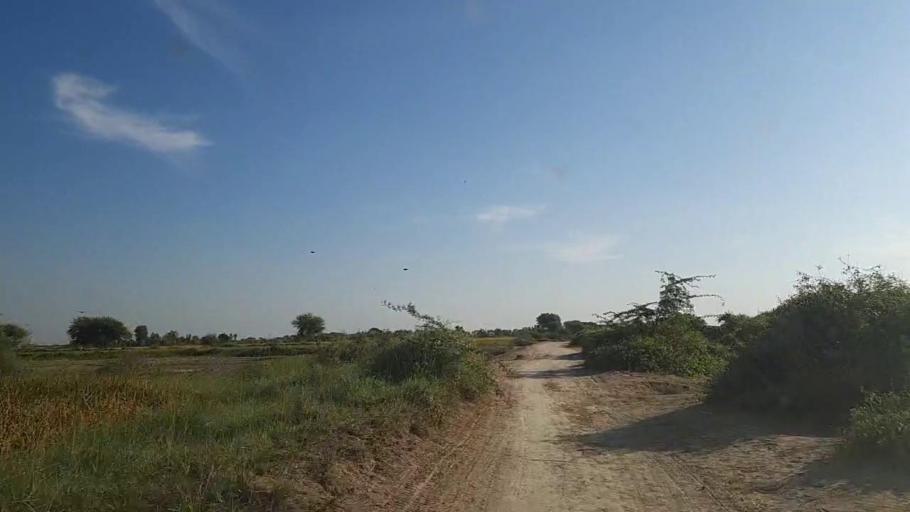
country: PK
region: Sindh
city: Mirpur Batoro
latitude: 24.7552
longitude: 68.3647
